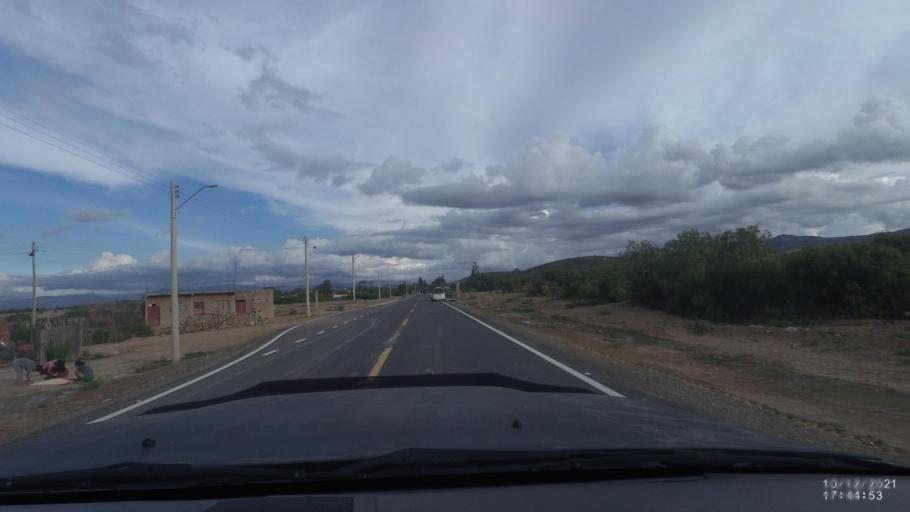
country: BO
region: Cochabamba
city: Tarata
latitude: -17.6227
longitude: -66.0074
